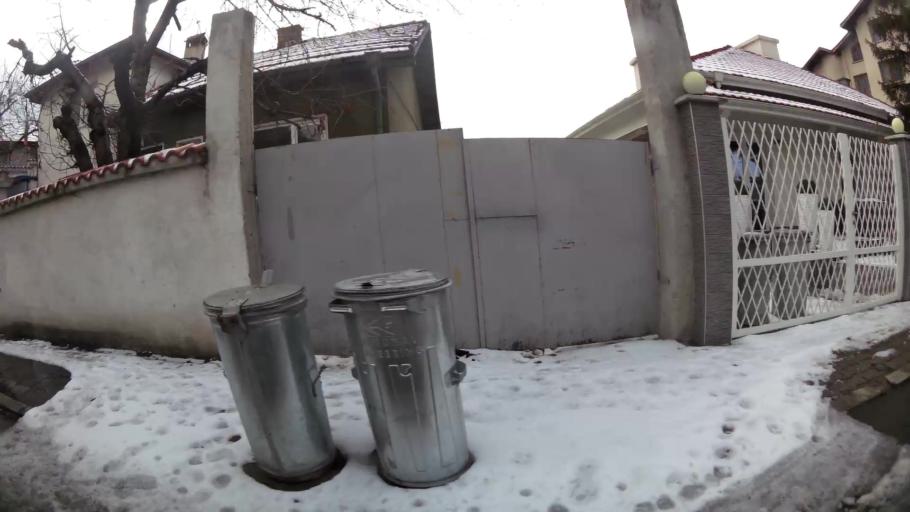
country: BG
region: Sofia-Capital
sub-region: Stolichna Obshtina
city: Sofia
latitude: 42.7005
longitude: 23.3867
